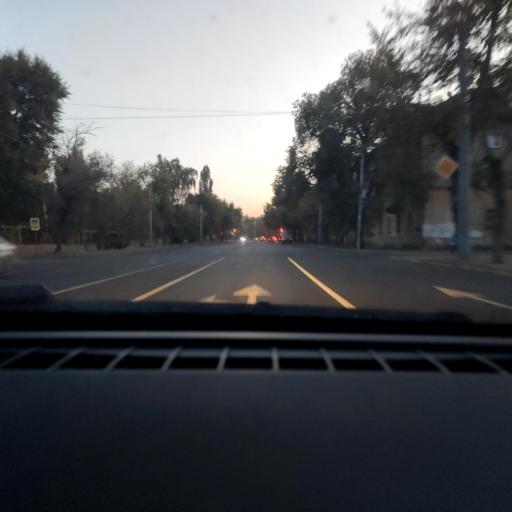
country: RU
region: Voronezj
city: Maslovka
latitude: 51.6170
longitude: 39.2488
